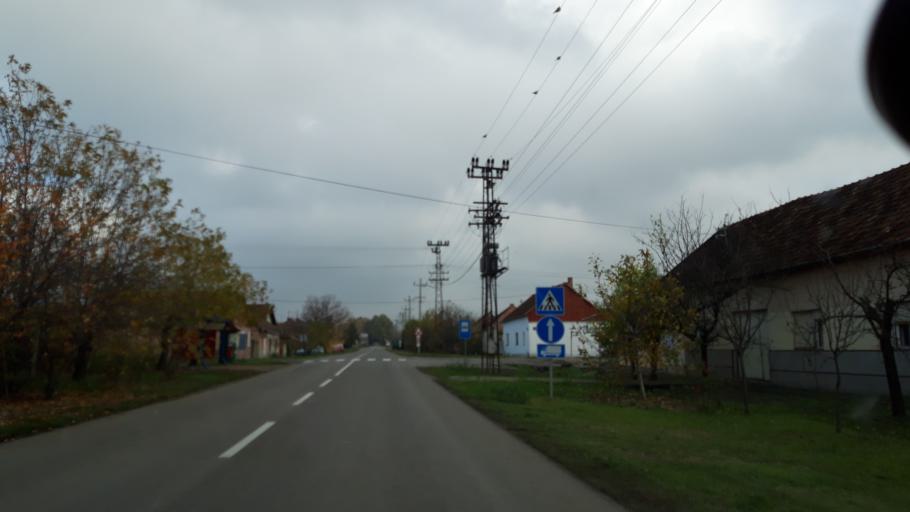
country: RS
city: Padej
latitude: 45.8286
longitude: 20.1677
